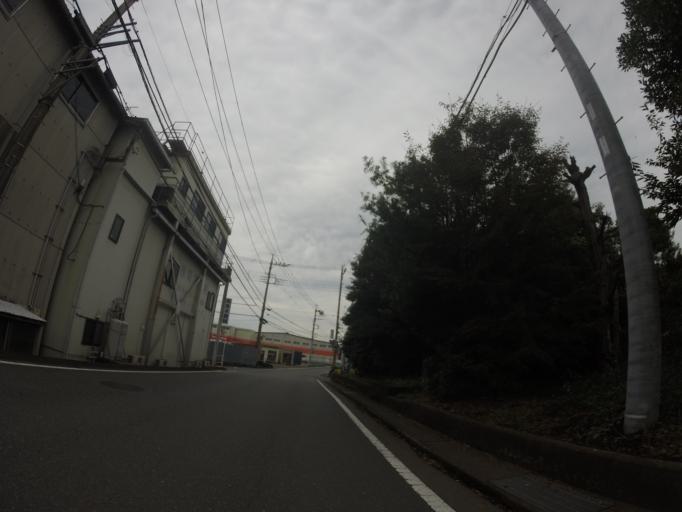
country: JP
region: Shizuoka
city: Fuji
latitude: 35.1977
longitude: 138.6766
